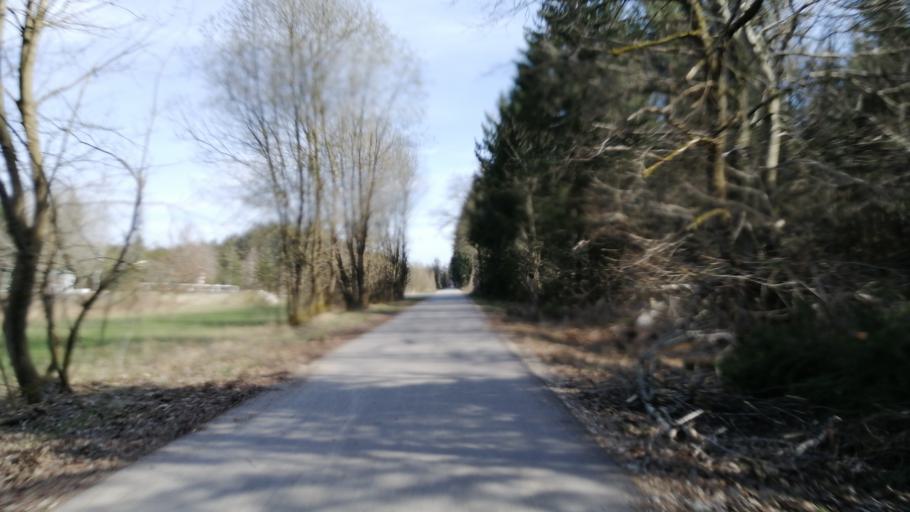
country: DE
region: Bavaria
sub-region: Upper Bavaria
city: Oberhaching
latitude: 47.9974
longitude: 11.6123
